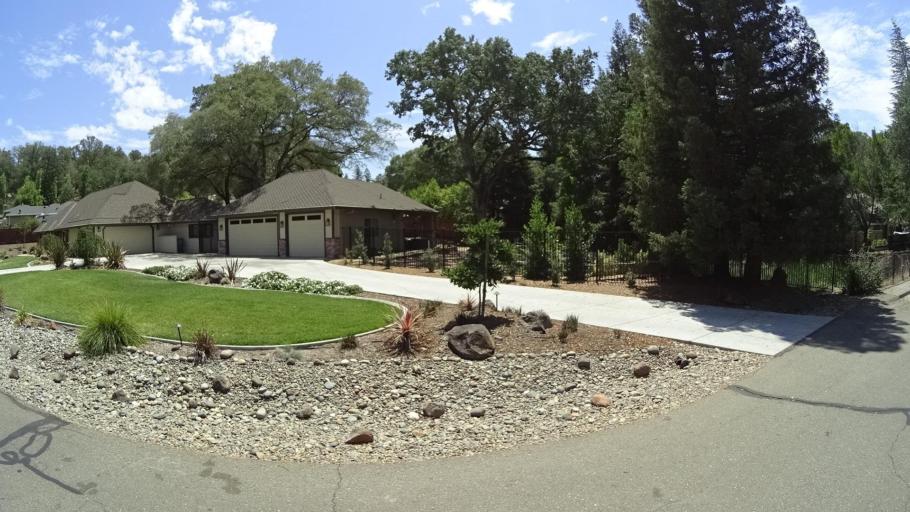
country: US
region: California
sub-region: Placer County
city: Rocklin
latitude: 38.8126
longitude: -121.2368
